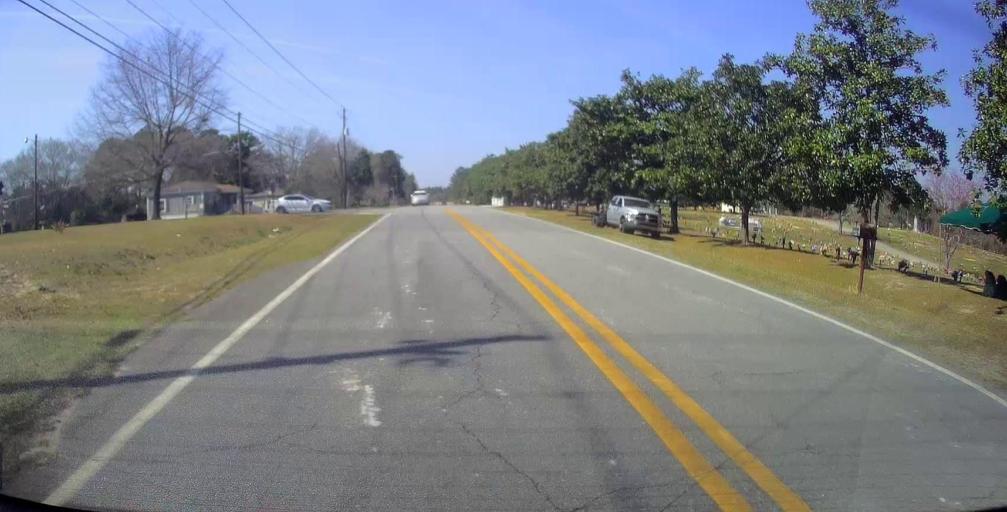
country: US
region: Georgia
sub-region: Bibb County
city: Macon
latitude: 32.8782
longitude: -83.5663
